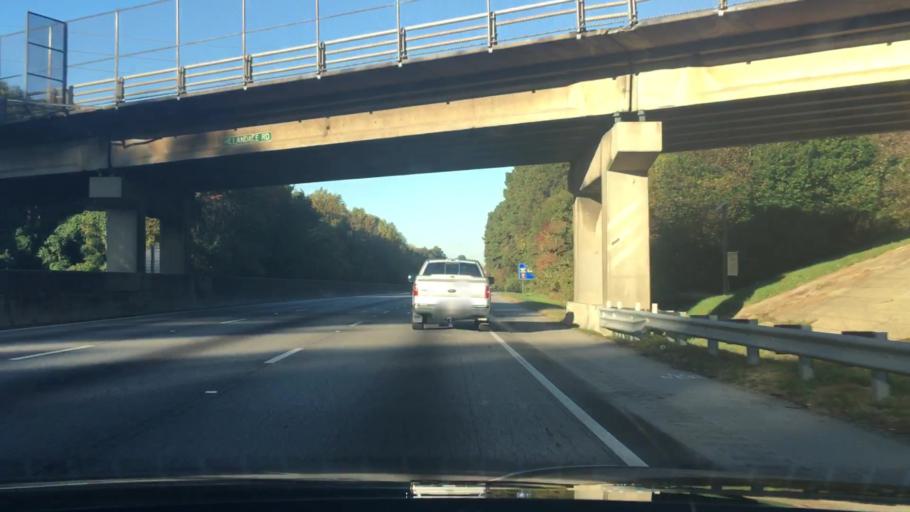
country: US
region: Georgia
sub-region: DeKalb County
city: Pine Mountain
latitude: 33.7033
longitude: -84.1462
